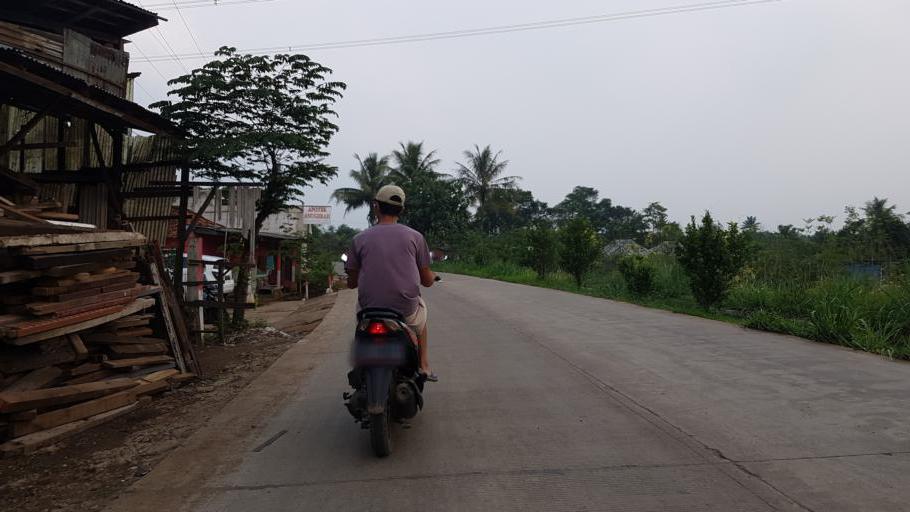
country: ID
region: West Java
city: Parung
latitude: -6.4626
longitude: 106.7070
